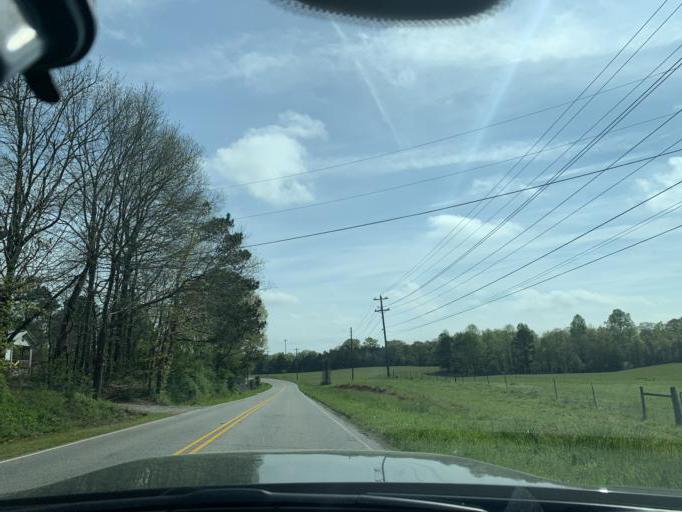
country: US
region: Georgia
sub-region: Forsyth County
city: Cumming
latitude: 34.2488
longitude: -84.0784
